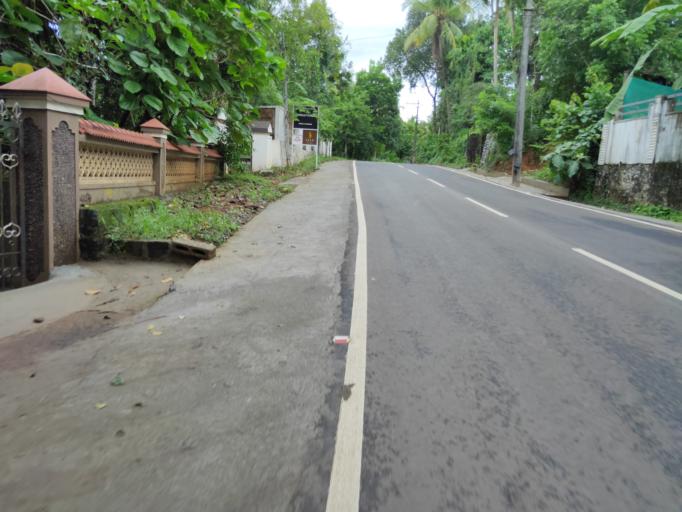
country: IN
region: Kerala
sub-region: Malappuram
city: Manjeri
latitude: 11.1858
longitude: 76.2084
